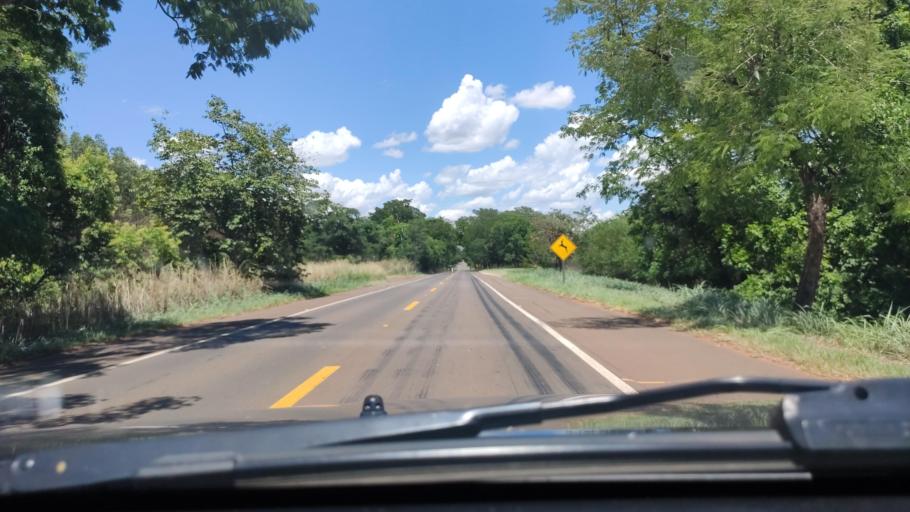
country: BR
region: Sao Paulo
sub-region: Boa Esperanca Do Sul
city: Boa Esperanca do Sul
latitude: -22.0691
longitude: -48.3752
